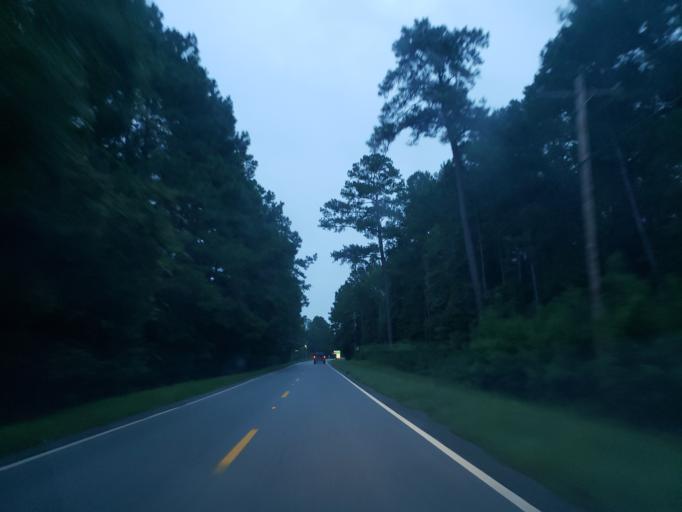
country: US
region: Georgia
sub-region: Chatham County
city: Bloomingdale
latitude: 32.0934
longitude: -81.3352
